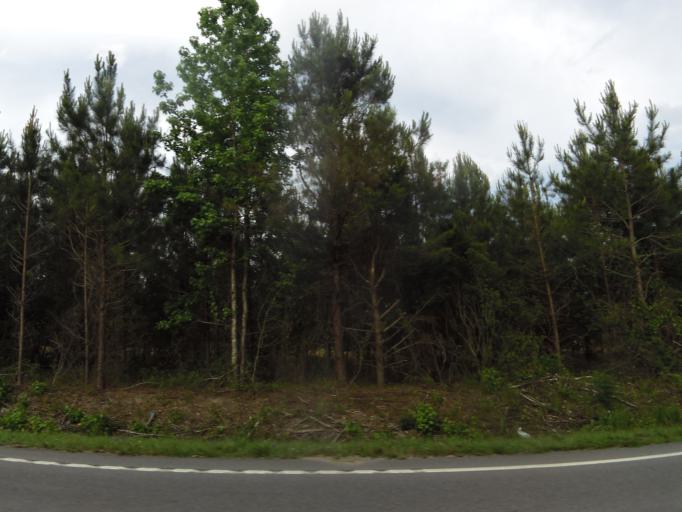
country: US
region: South Carolina
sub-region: Jasper County
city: Ridgeland
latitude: 32.4762
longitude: -81.1144
